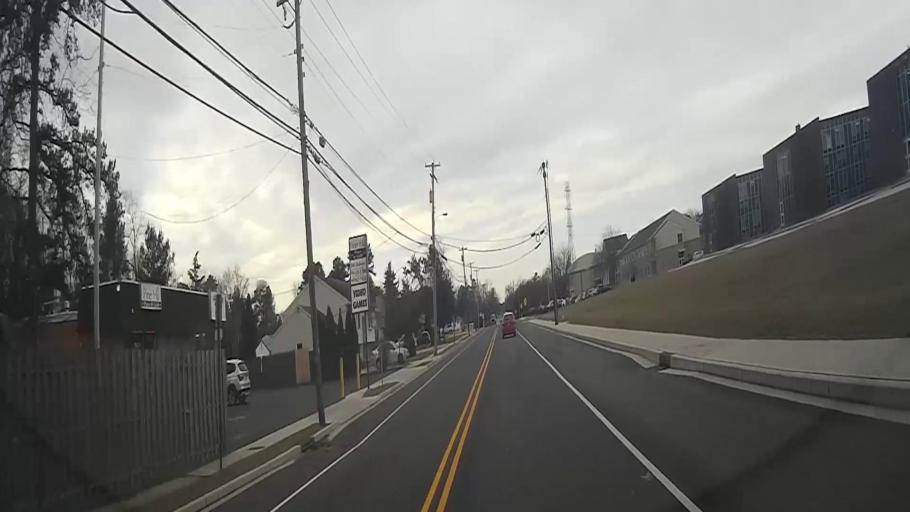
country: US
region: New Jersey
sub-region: Camden County
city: Pine Hill
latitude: 39.7766
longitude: -74.9659
